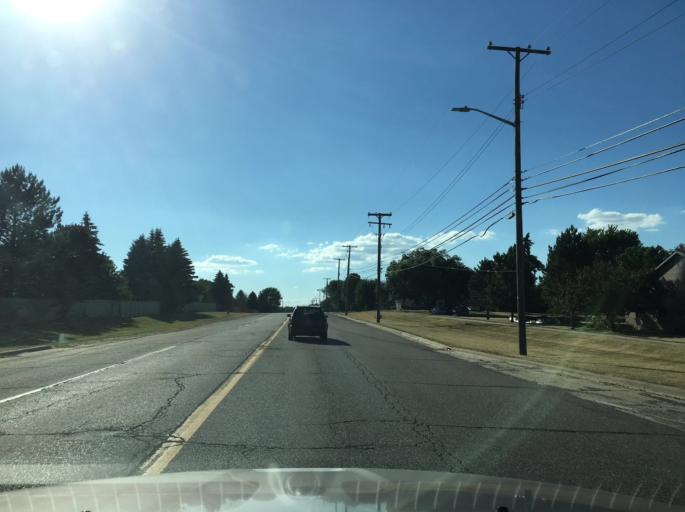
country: US
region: Michigan
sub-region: Macomb County
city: Fraser
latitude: 42.5728
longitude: -82.9790
